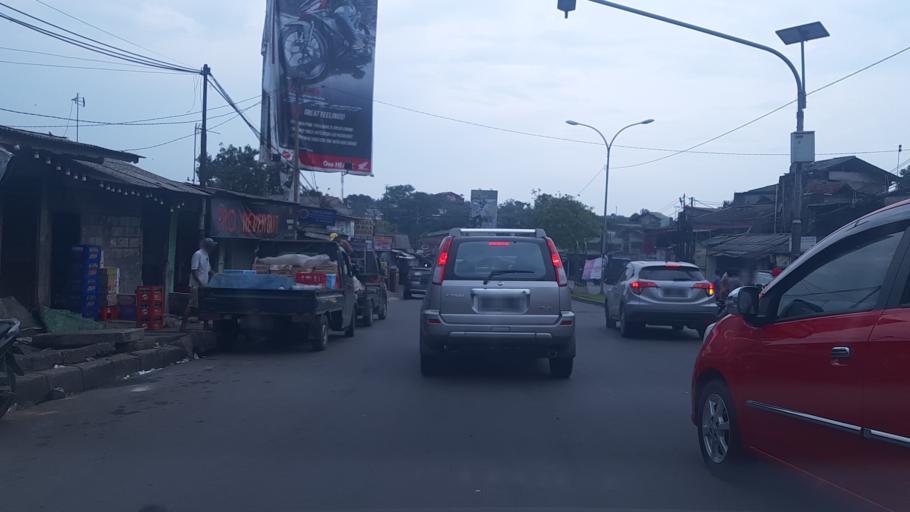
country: ID
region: West Java
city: Citeureup
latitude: -6.4811
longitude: 106.8690
